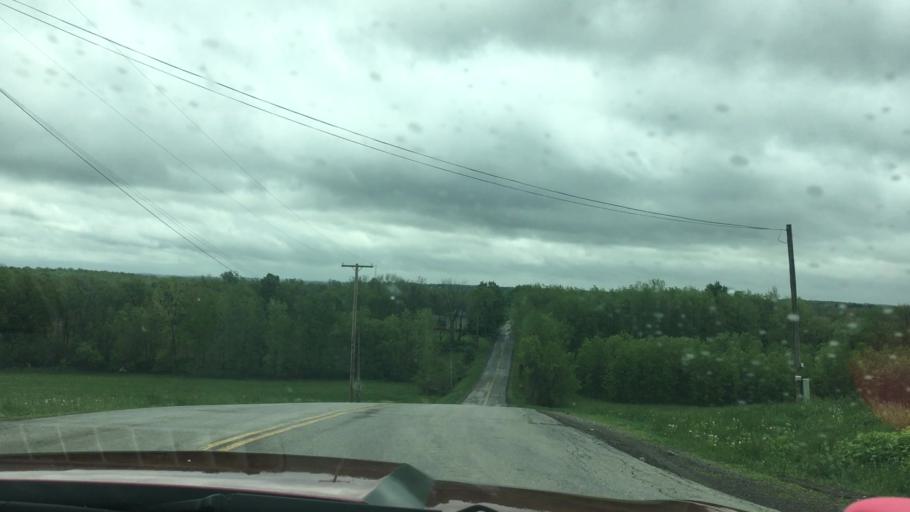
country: US
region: New York
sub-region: Genesee County
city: Batavia
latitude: 43.0839
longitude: -78.1395
